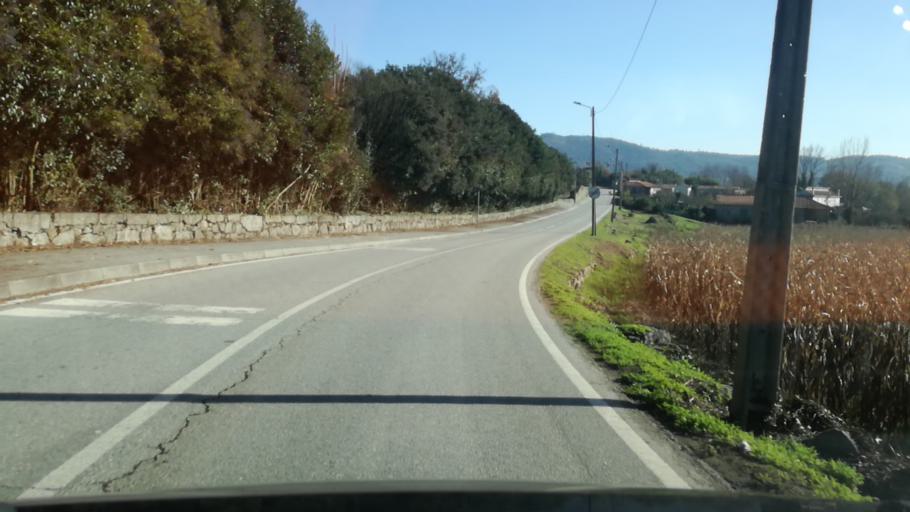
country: PT
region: Braga
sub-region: Guimaraes
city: Ponte
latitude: 41.5182
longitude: -8.3180
